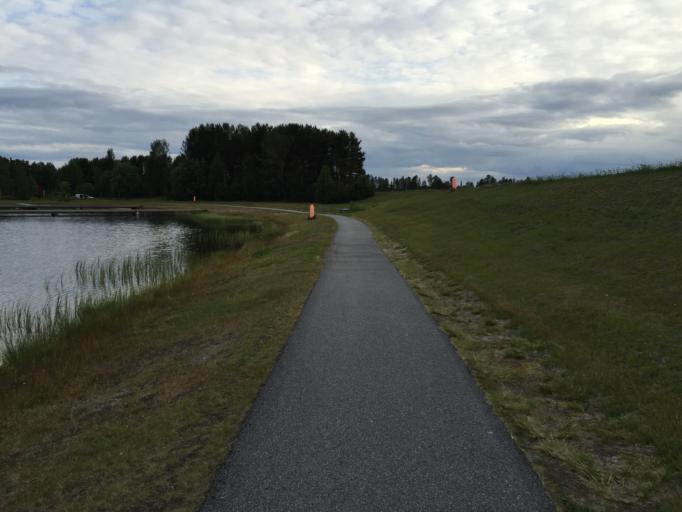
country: SE
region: Vaesterbotten
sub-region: Storumans Kommun
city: Storuman
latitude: 65.1030
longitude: 17.1122
